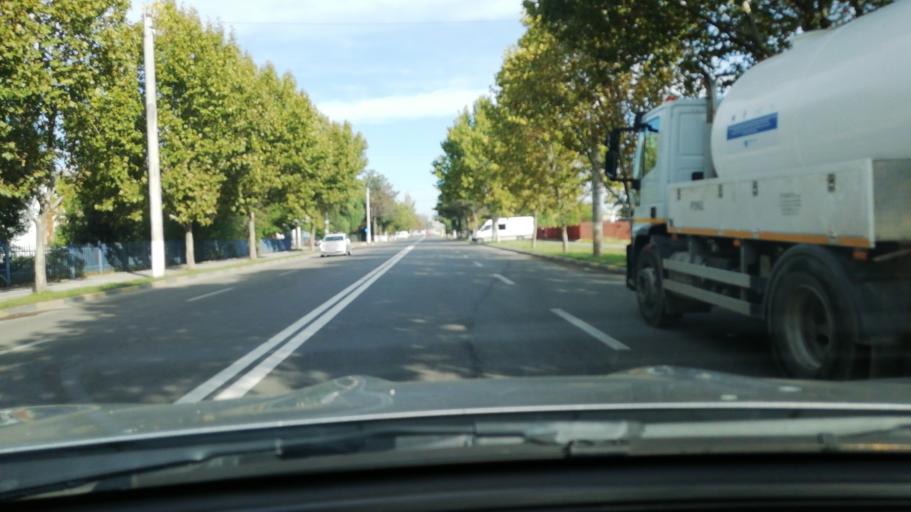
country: RO
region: Galati
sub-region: Municipiul Tecuci
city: Tecuci
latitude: 45.8211
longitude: 27.4390
